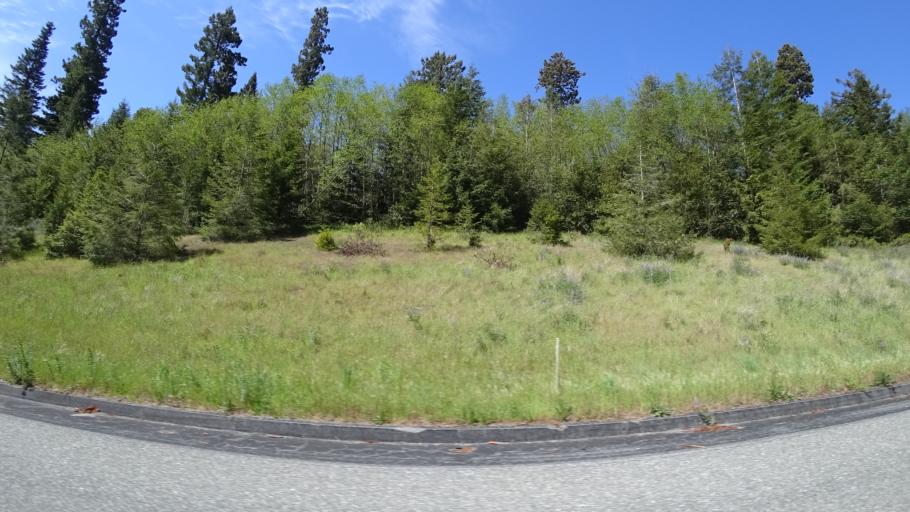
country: US
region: California
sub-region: Humboldt County
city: Westhaven-Moonstone
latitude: 41.3673
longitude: -123.9917
